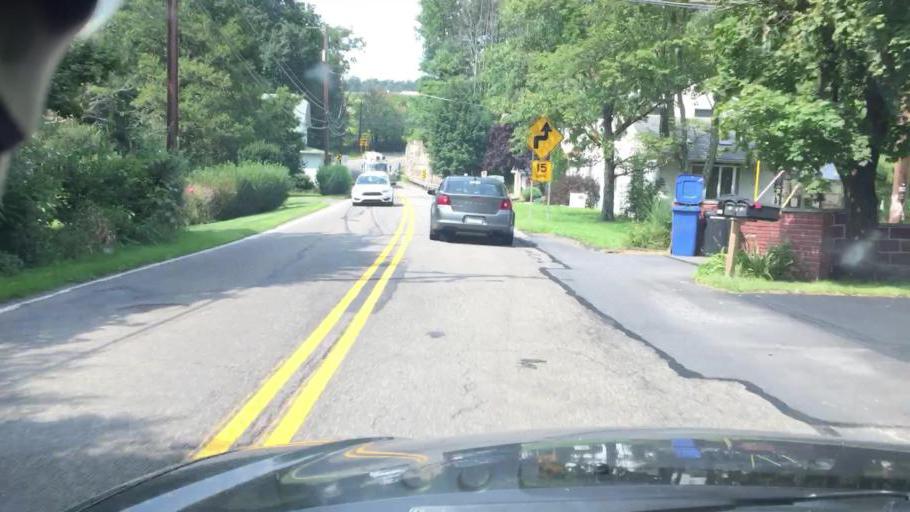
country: US
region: Pennsylvania
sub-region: Luzerne County
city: Harleigh
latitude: 41.0063
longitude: -75.9991
